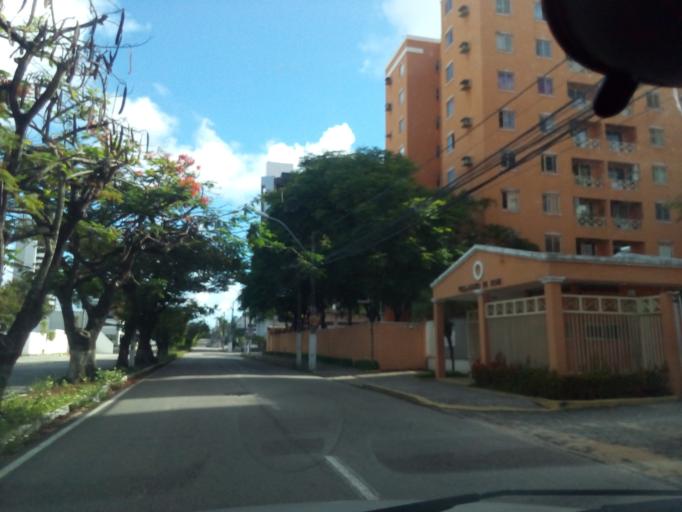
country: BR
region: Rio Grande do Norte
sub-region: Natal
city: Natal
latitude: -5.8190
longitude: -35.2108
